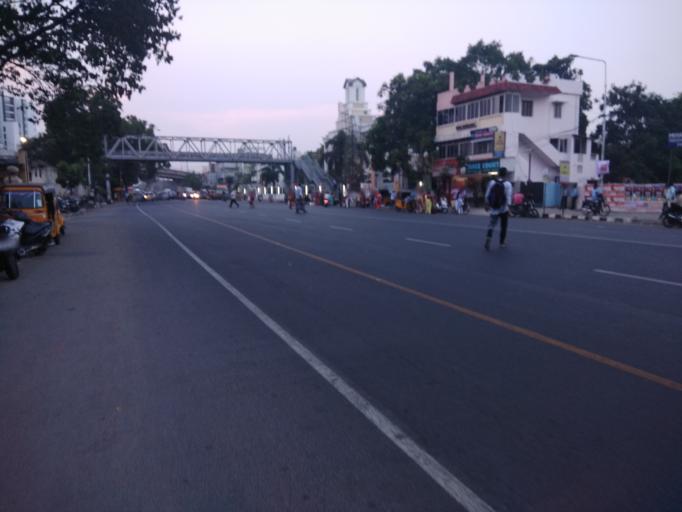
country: IN
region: Tamil Nadu
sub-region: Kancheepuram
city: Alandur
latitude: 13.0140
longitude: 80.2262
